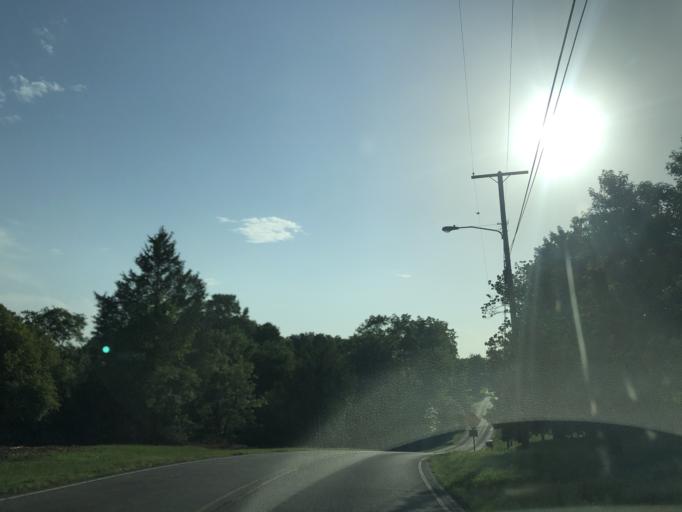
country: US
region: Tennessee
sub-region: Davidson County
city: Lakewood
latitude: 36.1498
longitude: -86.6567
